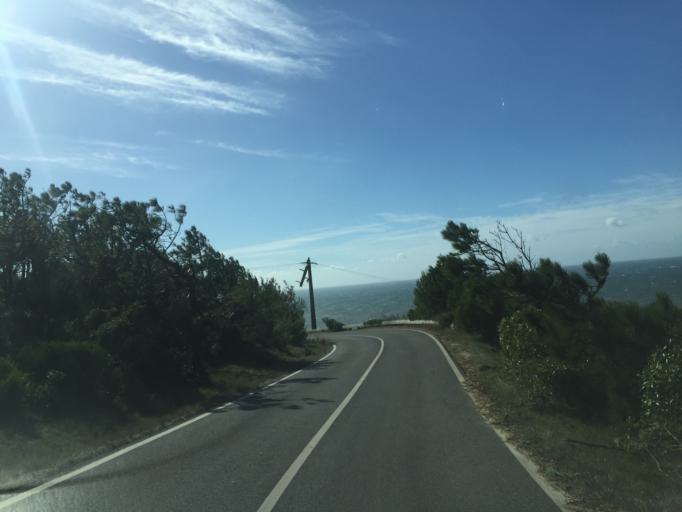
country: PT
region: Coimbra
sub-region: Figueira da Foz
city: Buarcos
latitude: 40.1826
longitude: -8.9048
